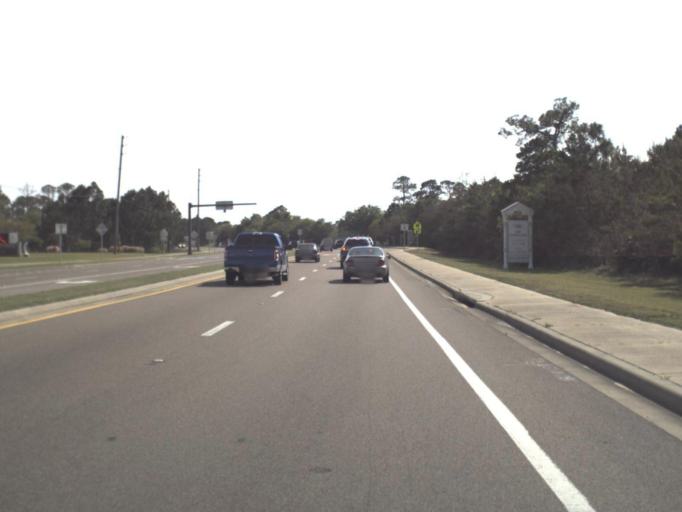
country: US
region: Florida
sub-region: Okaloosa County
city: Destin
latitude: 30.4005
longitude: -86.4267
